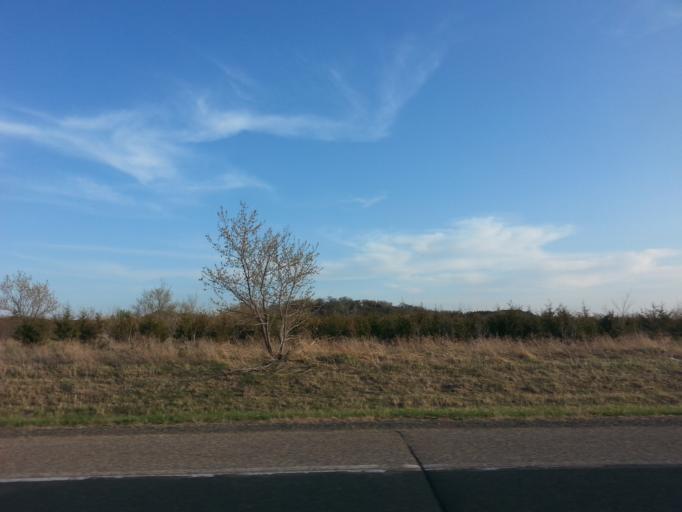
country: US
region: Minnesota
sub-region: Washington County
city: Lake Saint Croix Beach
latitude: 44.9310
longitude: -92.7012
